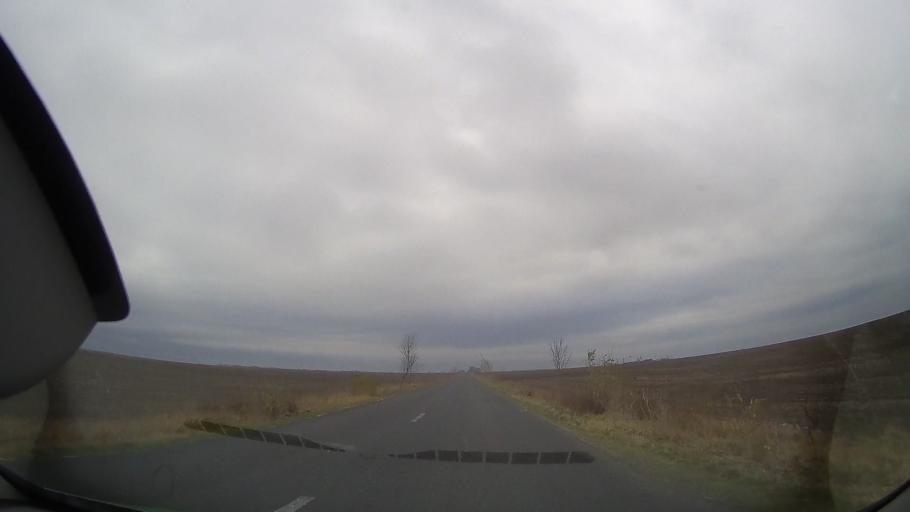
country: RO
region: Buzau
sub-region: Comuna Padina
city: Padina
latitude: 44.7988
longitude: 27.1369
